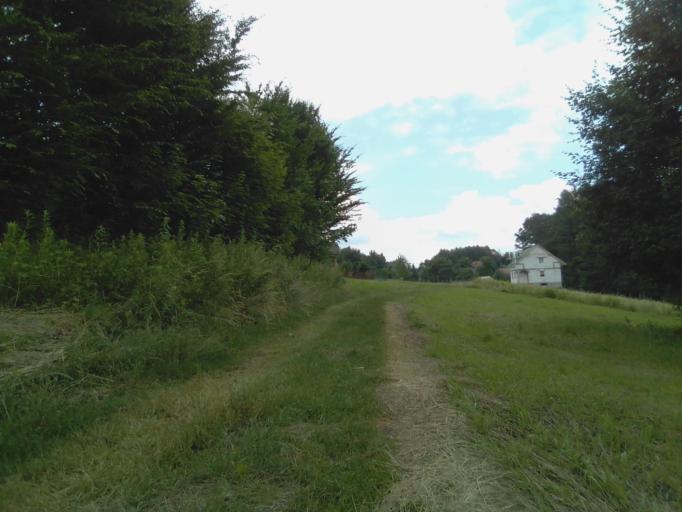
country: PL
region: Subcarpathian Voivodeship
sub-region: Powiat strzyzowski
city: Strzyzow
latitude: 49.8824
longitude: 21.7837
